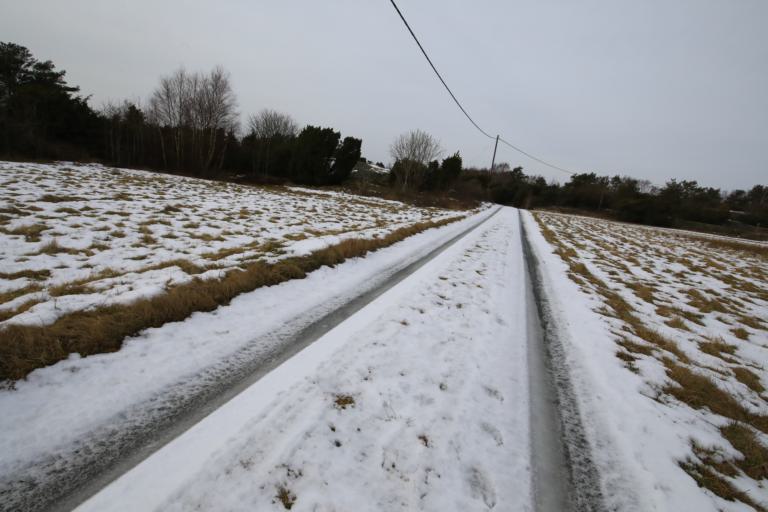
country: SE
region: Halland
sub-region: Kungsbacka Kommun
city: Frillesas
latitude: 57.2182
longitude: 12.1433
